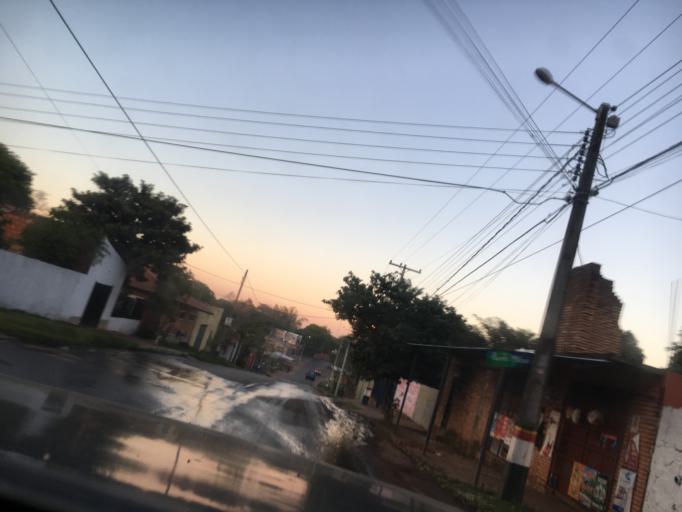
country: PY
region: Central
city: Villa Elisa
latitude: -25.3584
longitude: -57.5891
